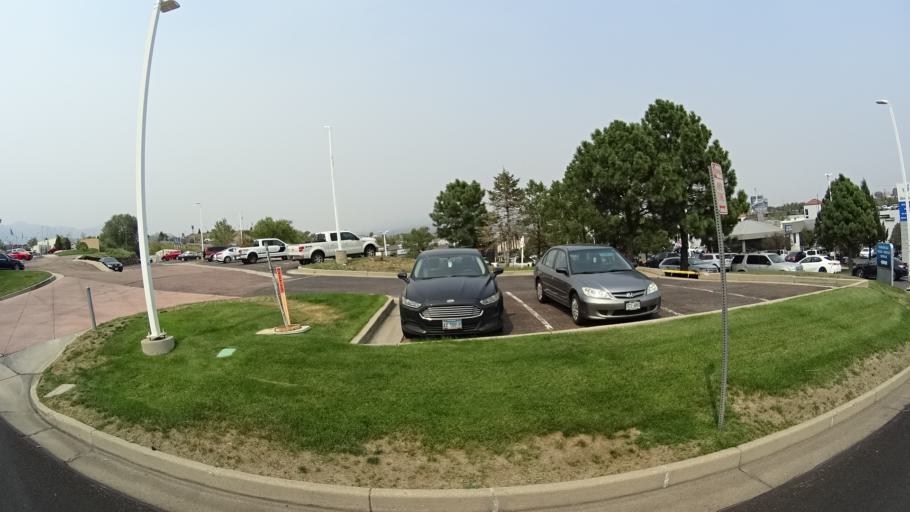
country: US
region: Colorado
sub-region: El Paso County
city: Colorado Springs
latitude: 38.8158
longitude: -104.8334
